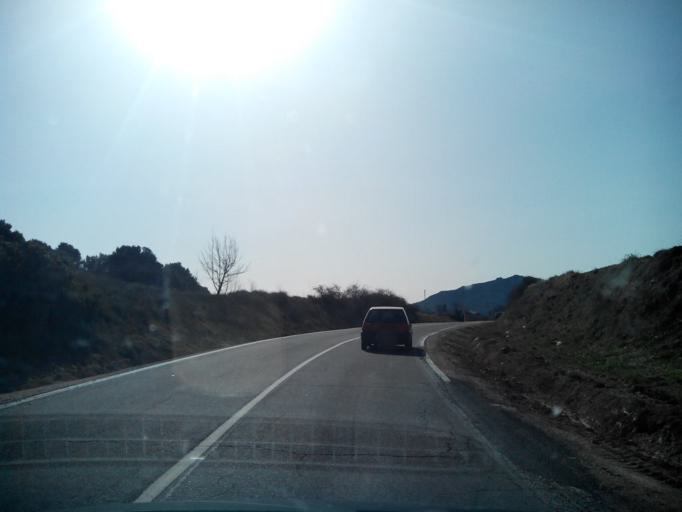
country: ES
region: Catalonia
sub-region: Provincia de Tarragona
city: Conesa
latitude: 41.5021
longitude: 1.3397
